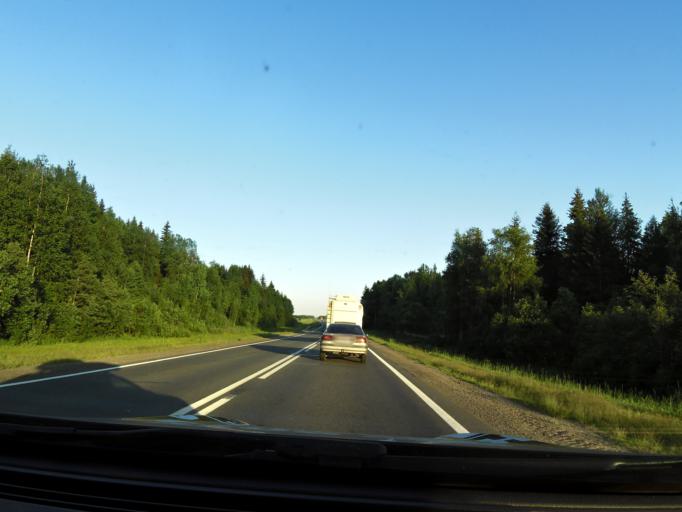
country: RU
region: Vologda
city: Gryazovets
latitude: 58.8346
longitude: 40.2097
